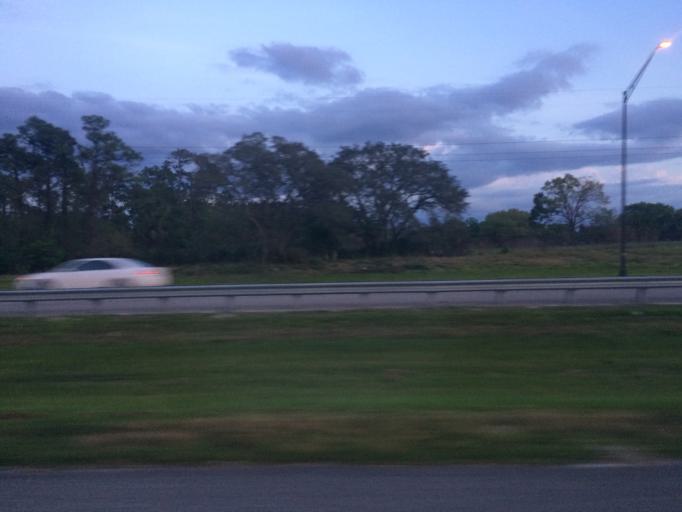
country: US
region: Florida
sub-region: Polk County
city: Loughman
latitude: 28.2910
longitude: -81.5848
